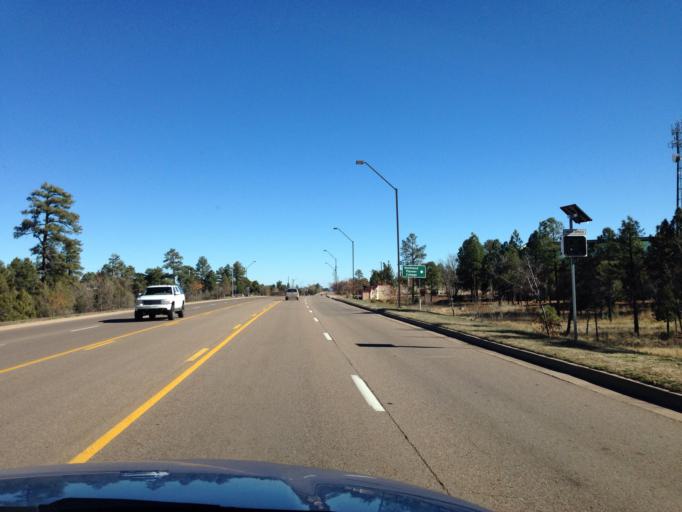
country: US
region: Arizona
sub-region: Navajo County
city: Show Low
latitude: 34.2428
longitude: -110.0562
